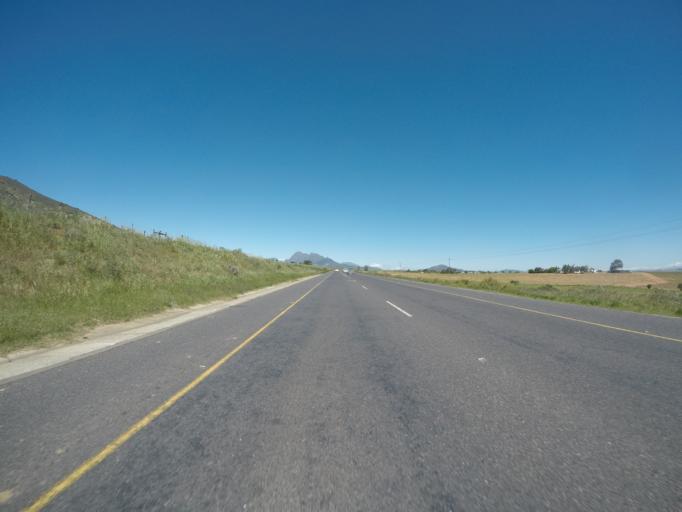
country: ZA
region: Western Cape
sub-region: Cape Winelands District Municipality
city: Noorder-Paarl
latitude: -33.7327
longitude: 18.8911
